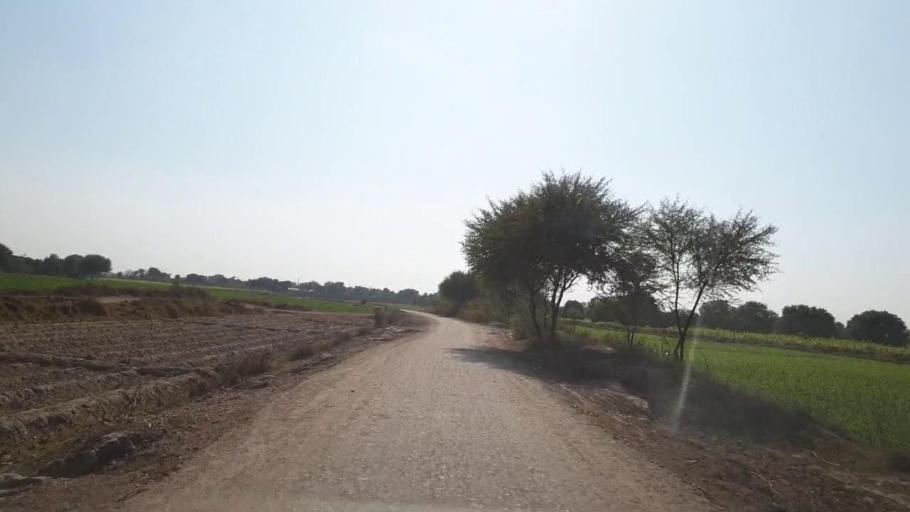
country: PK
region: Sindh
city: Tando Jam
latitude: 25.4995
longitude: 68.5003
